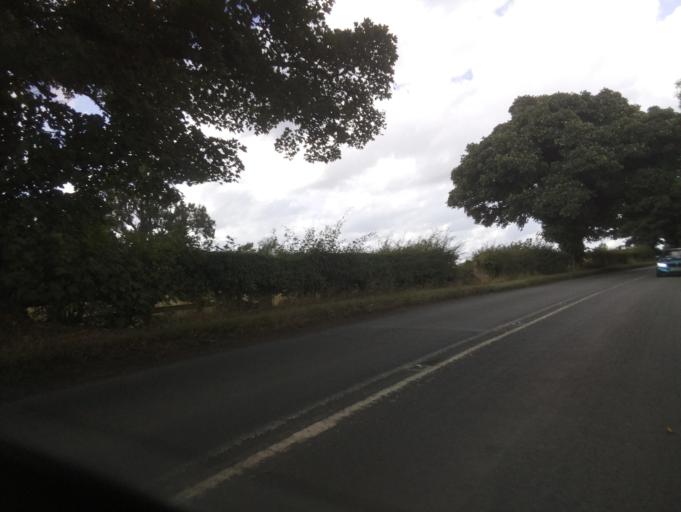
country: GB
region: England
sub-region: North Yorkshire
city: Bedale
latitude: 54.2292
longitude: -1.6658
